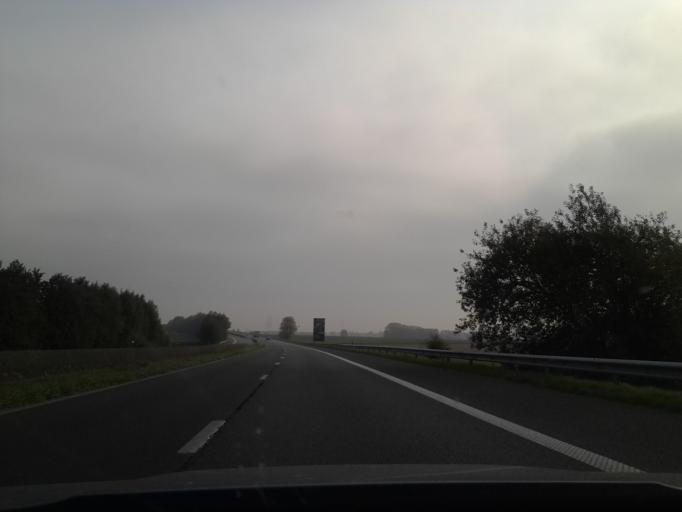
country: BE
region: Wallonia
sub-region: Province du Hainaut
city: Celles
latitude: 50.6534
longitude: 3.4947
